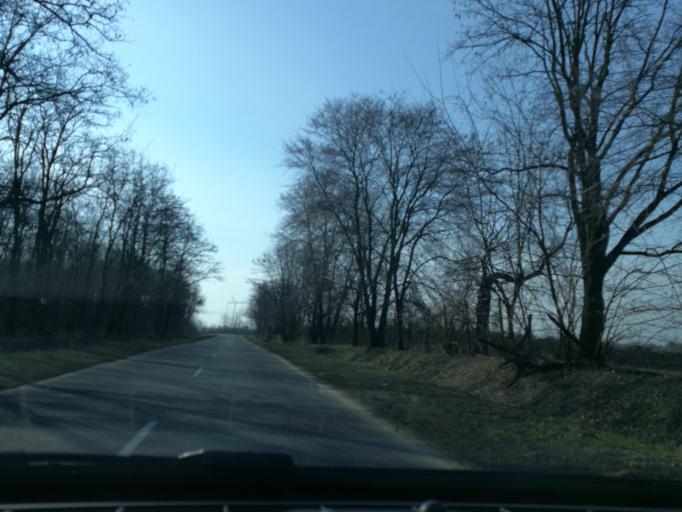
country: HU
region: Szabolcs-Szatmar-Bereg
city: Levelek
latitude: 47.9834
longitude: 21.9698
